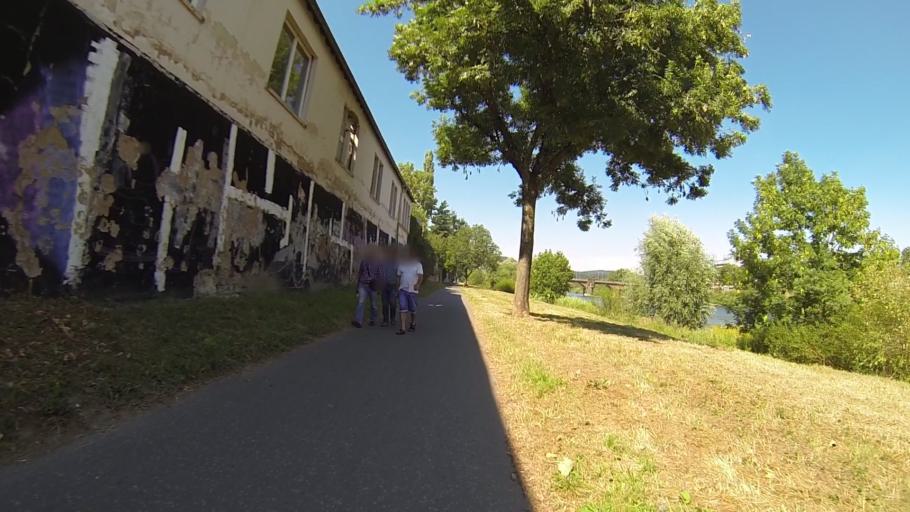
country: DE
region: Rheinland-Pfalz
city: Trier
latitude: 49.7488
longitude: 6.6250
